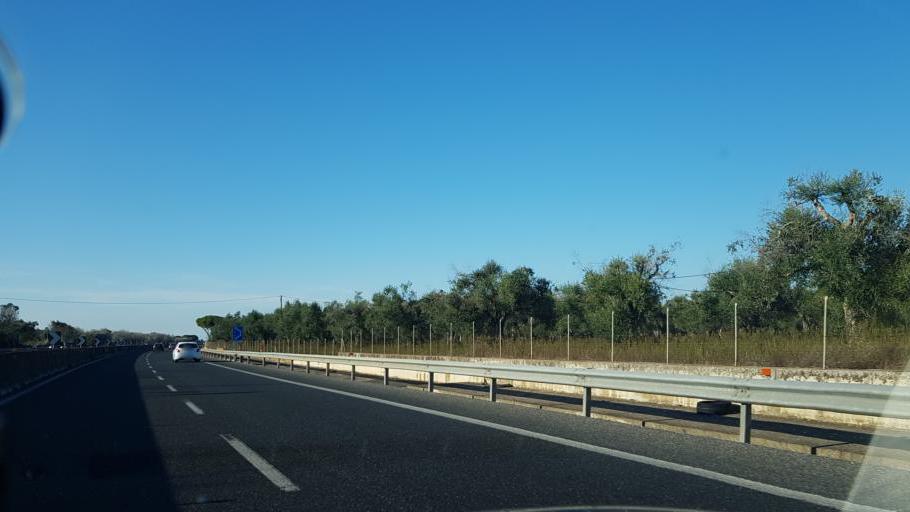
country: IT
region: Apulia
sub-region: Provincia di Brindisi
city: Torchiarolo
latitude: 40.4679
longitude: 18.0531
